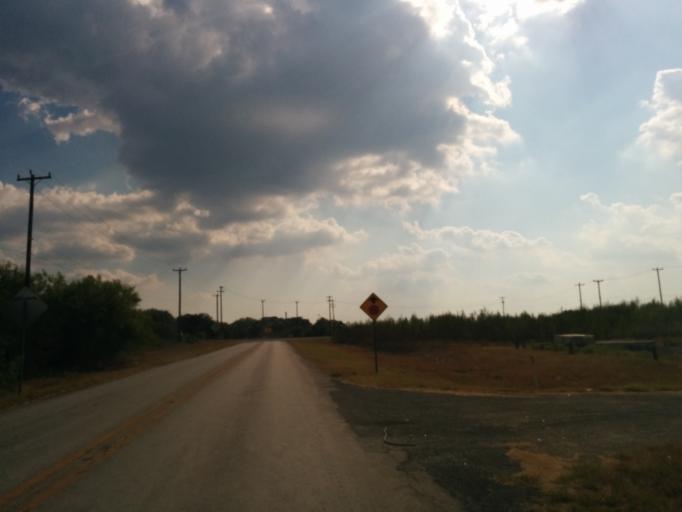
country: US
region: Texas
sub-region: Bexar County
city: Elmendorf
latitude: 29.2654
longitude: -98.3073
